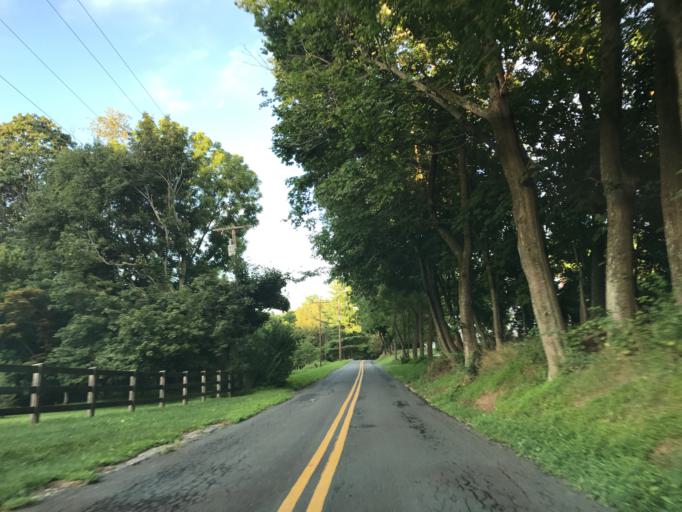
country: US
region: Pennsylvania
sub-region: York County
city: New Freedom
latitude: 39.7144
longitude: -76.6959
